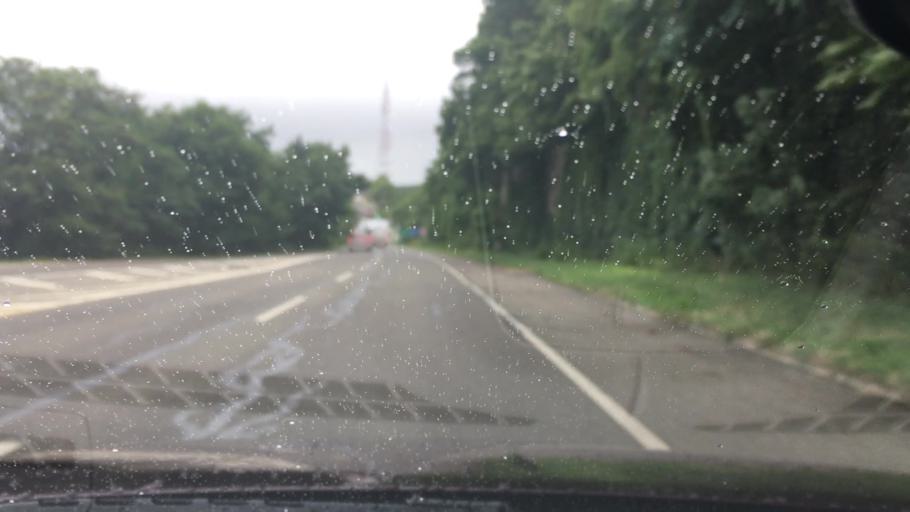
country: US
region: New York
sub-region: Suffolk County
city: Hauppauge
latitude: 40.8096
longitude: -73.2137
